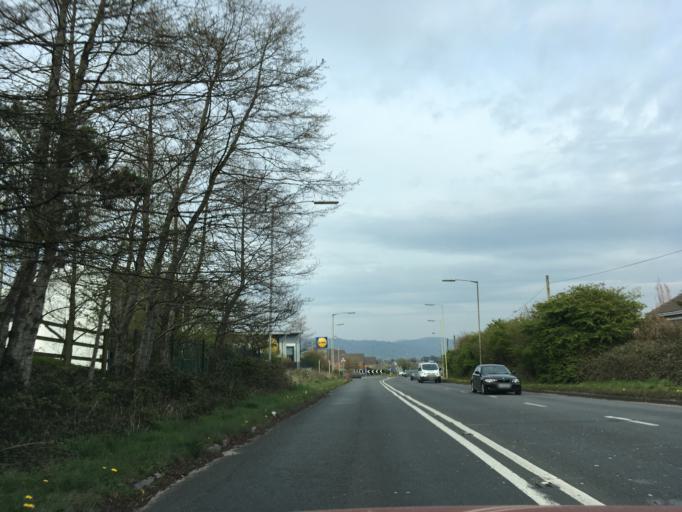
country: GB
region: Wales
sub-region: Caerphilly County Borough
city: Caerphilly
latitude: 51.5701
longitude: -3.2455
